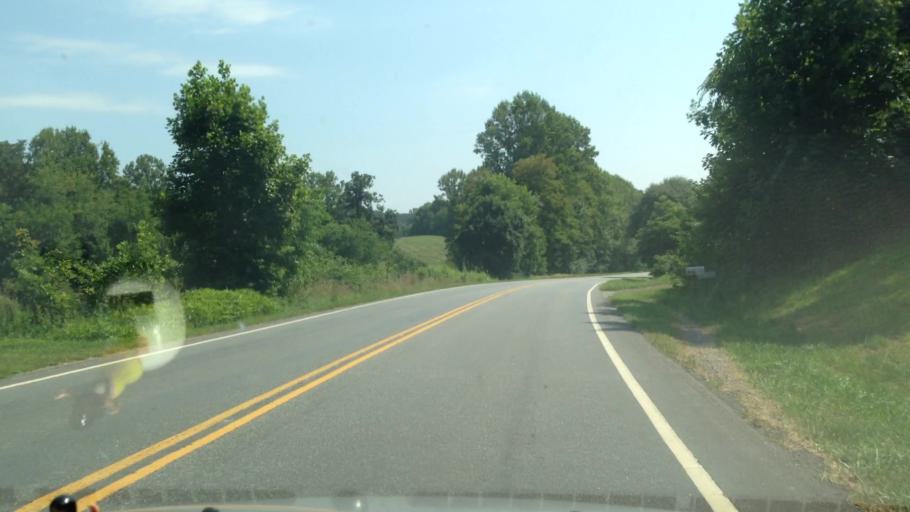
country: US
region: North Carolina
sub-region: Surry County
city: Flat Rock
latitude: 36.5567
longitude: -80.4755
